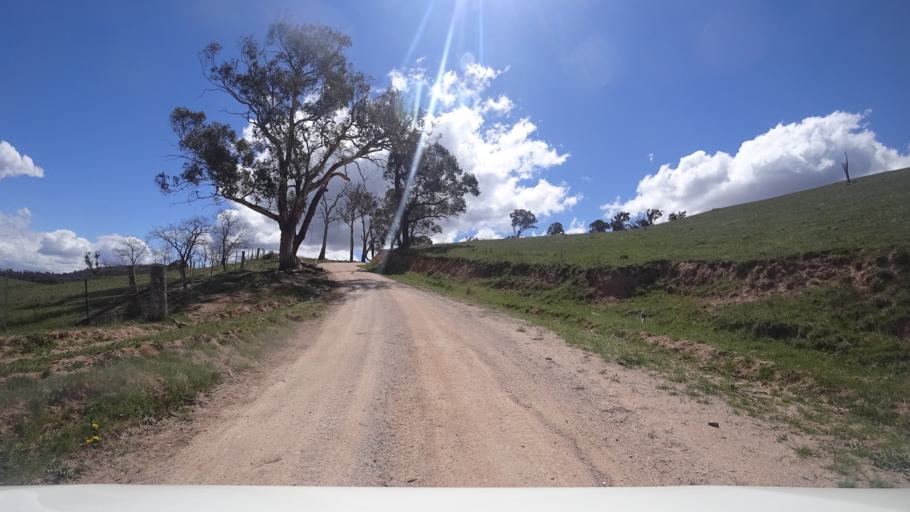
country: AU
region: New South Wales
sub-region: Oberon
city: Oberon
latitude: -33.5736
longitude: 149.9414
